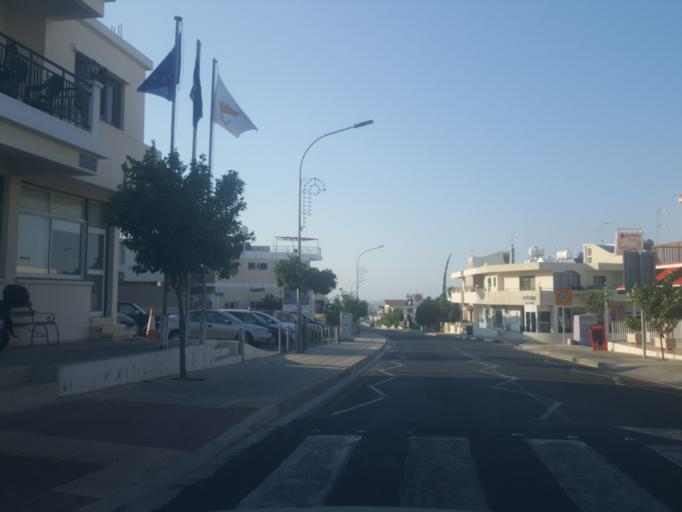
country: CY
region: Ammochostos
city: Deryneia
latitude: 35.0668
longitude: 33.9609
